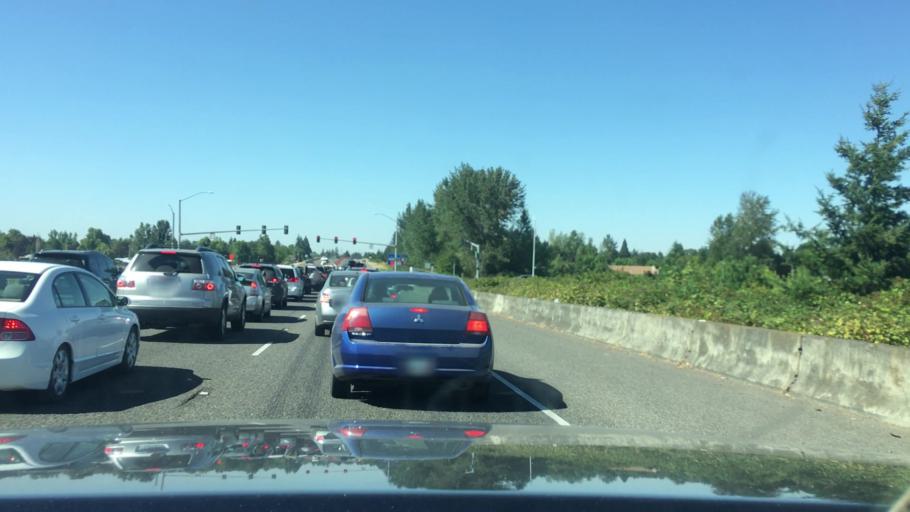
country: US
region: Oregon
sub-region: Lane County
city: Eugene
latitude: 44.0633
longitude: -123.1735
